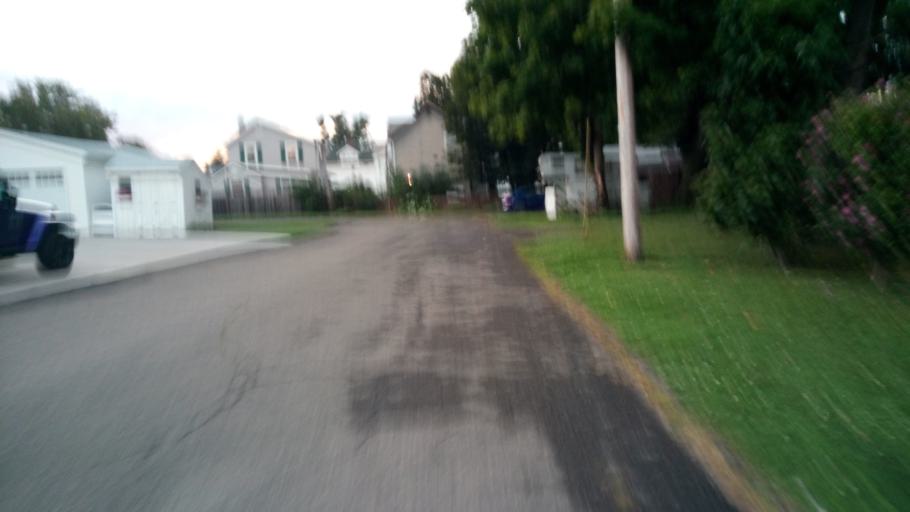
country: US
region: New York
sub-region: Chemung County
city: Elmira
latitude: 42.0944
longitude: -76.8196
